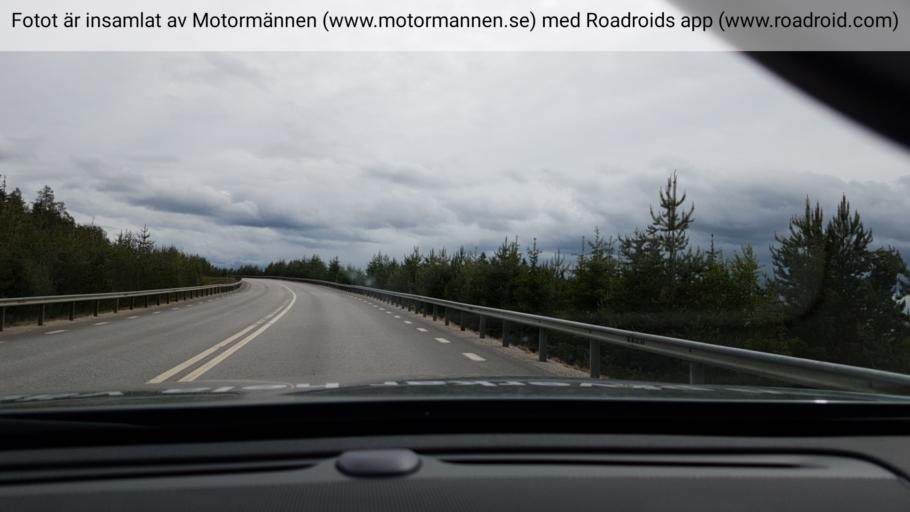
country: SE
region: Vaesterbotten
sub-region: Vannas Kommun
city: Vaennaes
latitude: 64.0096
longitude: 19.6985
